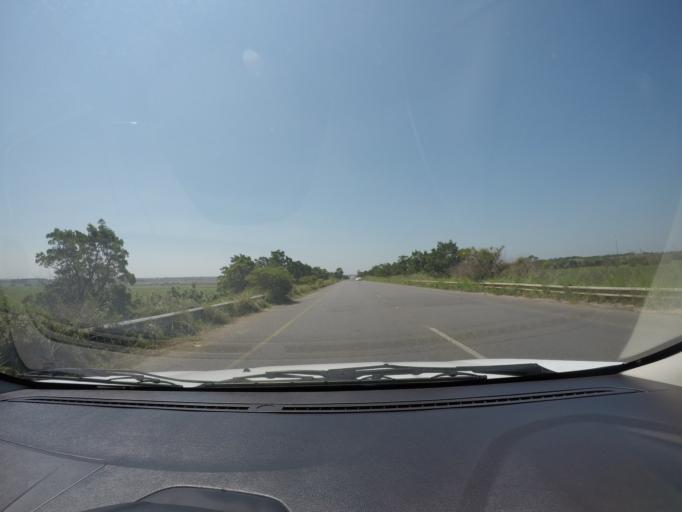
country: ZA
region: KwaZulu-Natal
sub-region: uThungulu District Municipality
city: Empangeni
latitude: -28.7824
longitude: 31.9580
